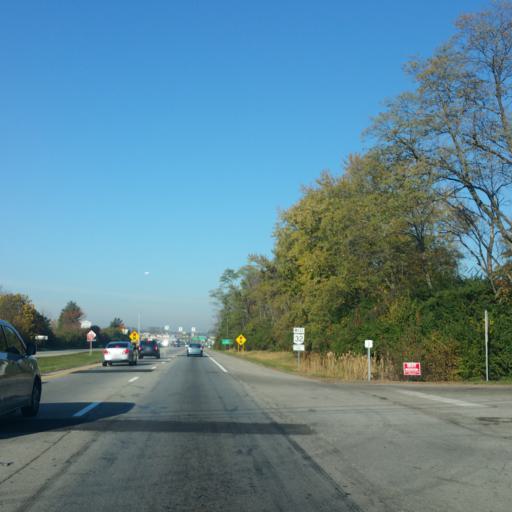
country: US
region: Ohio
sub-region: Clermont County
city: Summerside
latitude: 39.0935
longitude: -84.2578
